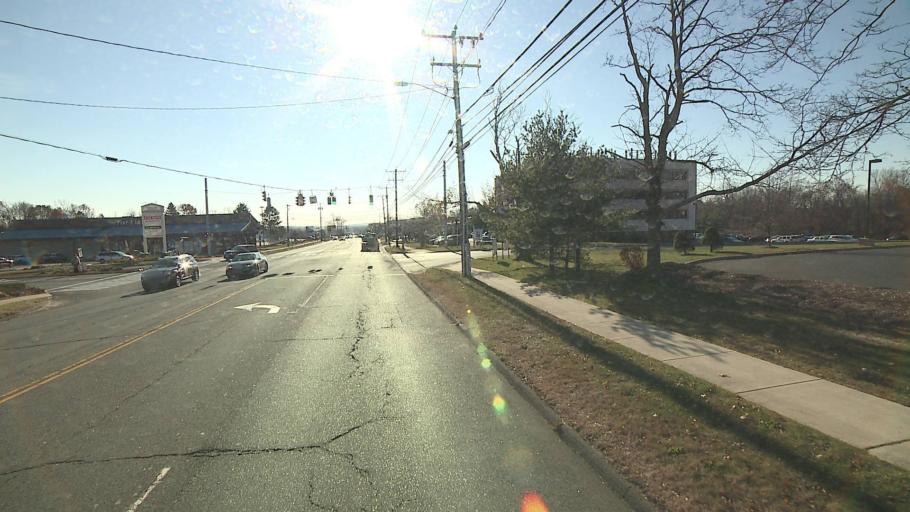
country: US
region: Connecticut
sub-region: New Haven County
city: Meriden
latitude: 41.5087
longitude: -72.8085
